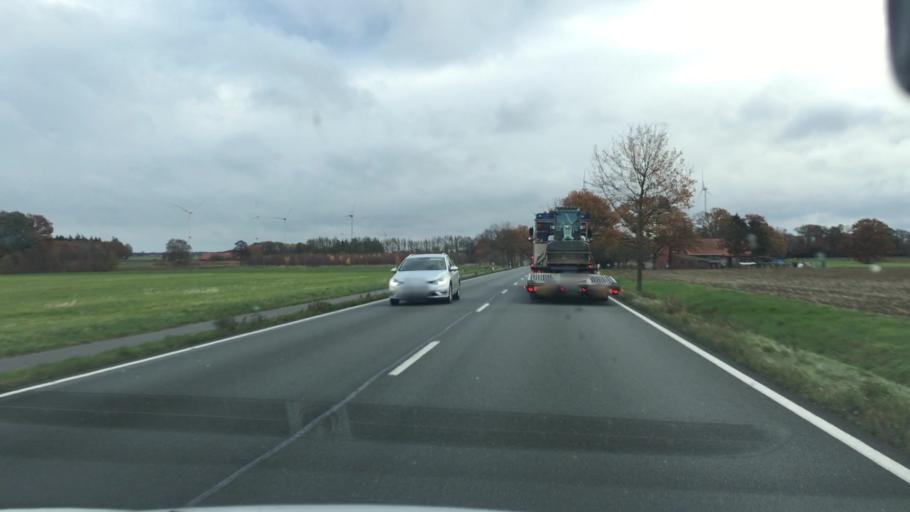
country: DE
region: Lower Saxony
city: Maasen
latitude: 52.6761
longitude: 8.9122
